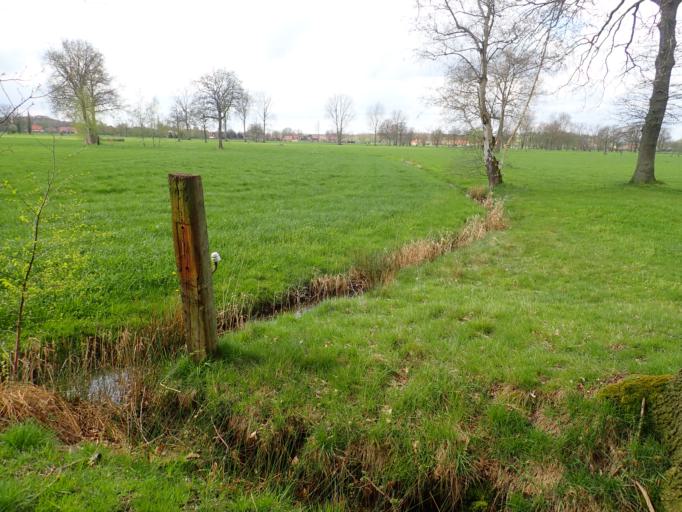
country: BE
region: Flanders
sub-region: Provincie Antwerpen
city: Vorselaar
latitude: 51.2246
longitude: 4.7888
